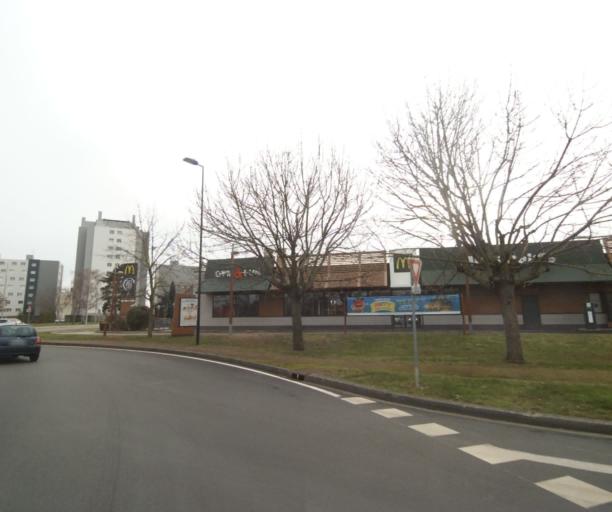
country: FR
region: Rhone-Alpes
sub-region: Departement de la Loire
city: Riorges
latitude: 46.0457
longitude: 4.0557
